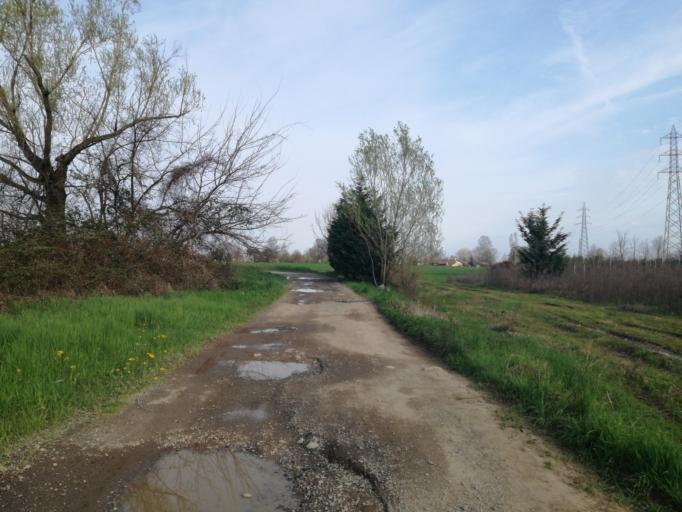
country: IT
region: Lombardy
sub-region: Provincia di Lecco
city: Verderio Superiore
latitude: 45.6690
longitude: 9.4521
